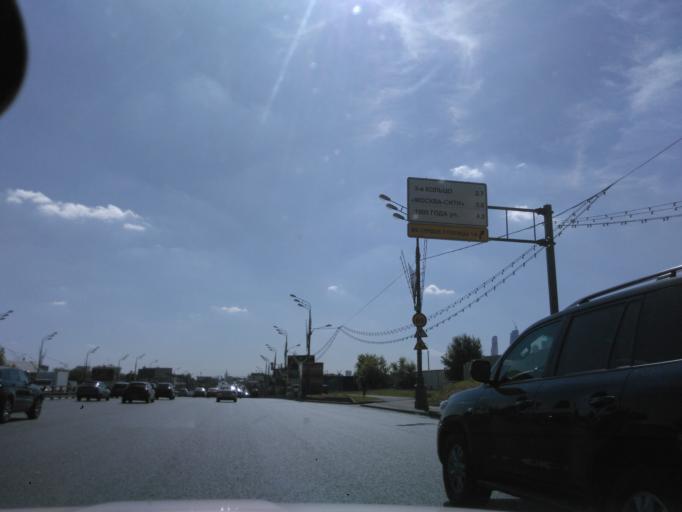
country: RU
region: Moskovskaya
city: Khoroshevo-Mnevniki
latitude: 55.7720
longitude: 37.4953
